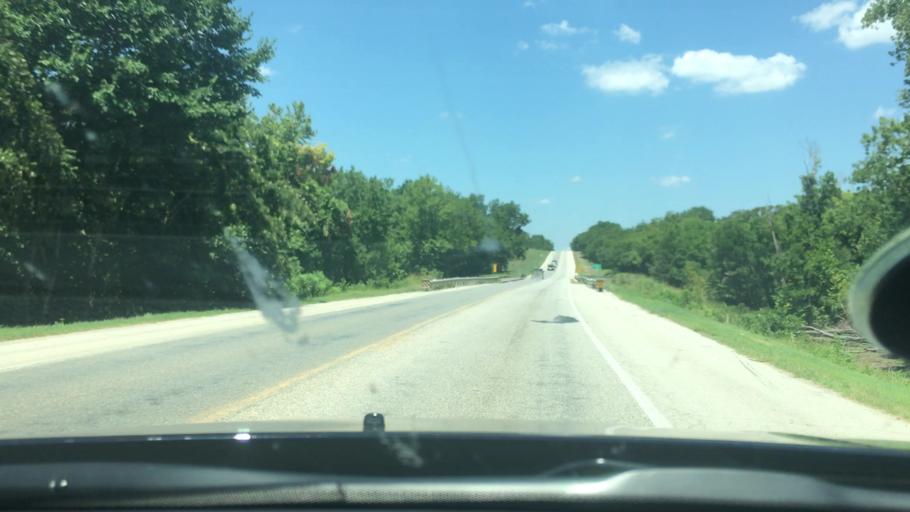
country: US
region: Oklahoma
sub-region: Marshall County
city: Oakland
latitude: 34.1750
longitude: -96.8571
